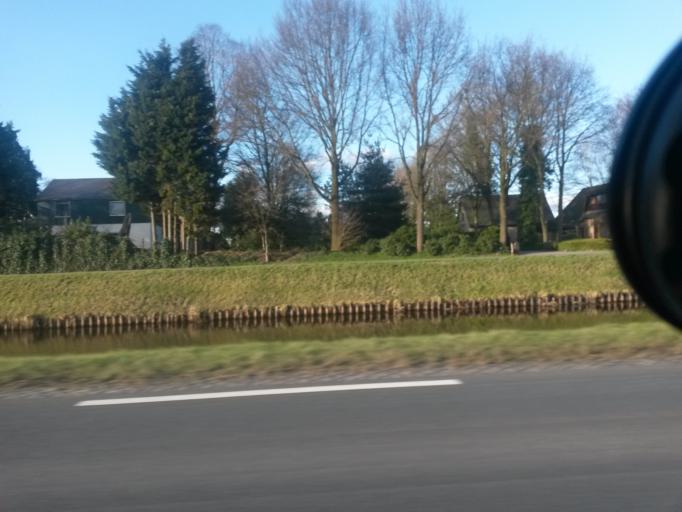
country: NL
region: Overijssel
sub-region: Gemeente Hardenberg
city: Hardenberg
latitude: 52.6537
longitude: 6.6515
